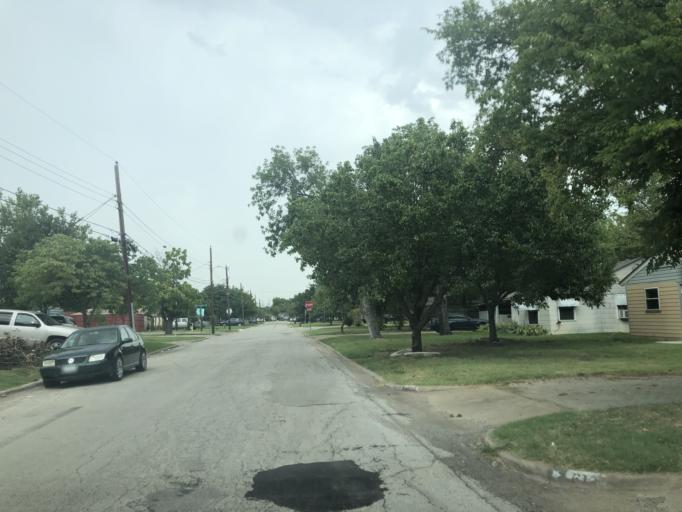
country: US
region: Texas
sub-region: Dallas County
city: Grand Prairie
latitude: 32.7386
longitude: -97.0137
